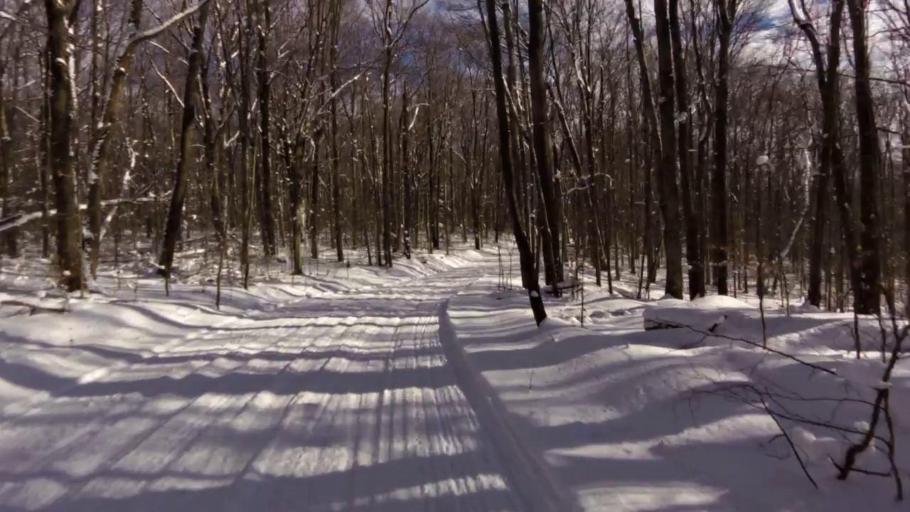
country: US
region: New York
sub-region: Cattaraugus County
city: Salamanca
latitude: 42.0742
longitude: -78.6873
